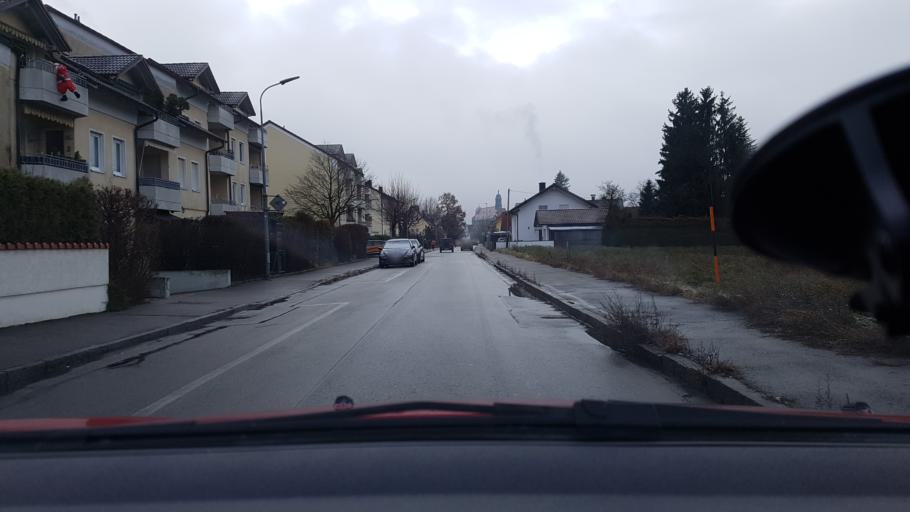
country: DE
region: Bavaria
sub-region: Upper Bavaria
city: Altoetting
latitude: 48.2342
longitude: 12.6708
